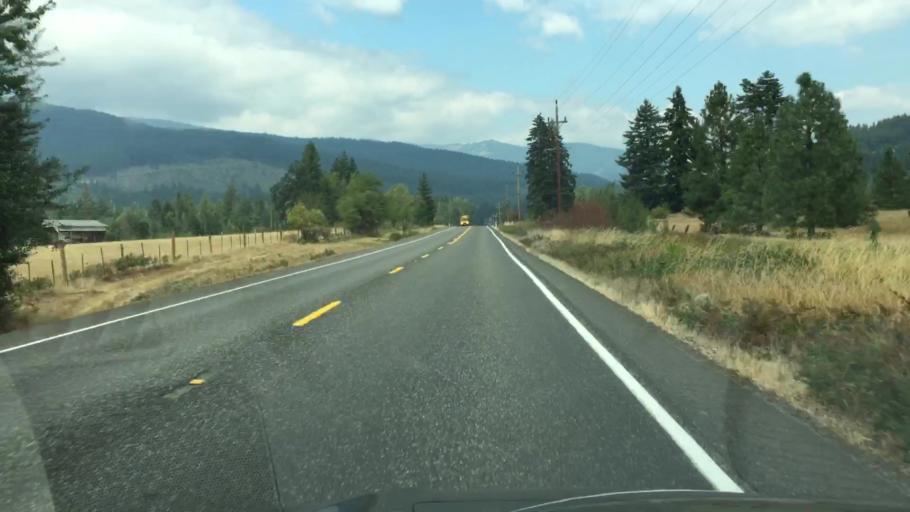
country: US
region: Washington
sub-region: Klickitat County
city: White Salmon
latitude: 45.8393
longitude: -121.5010
